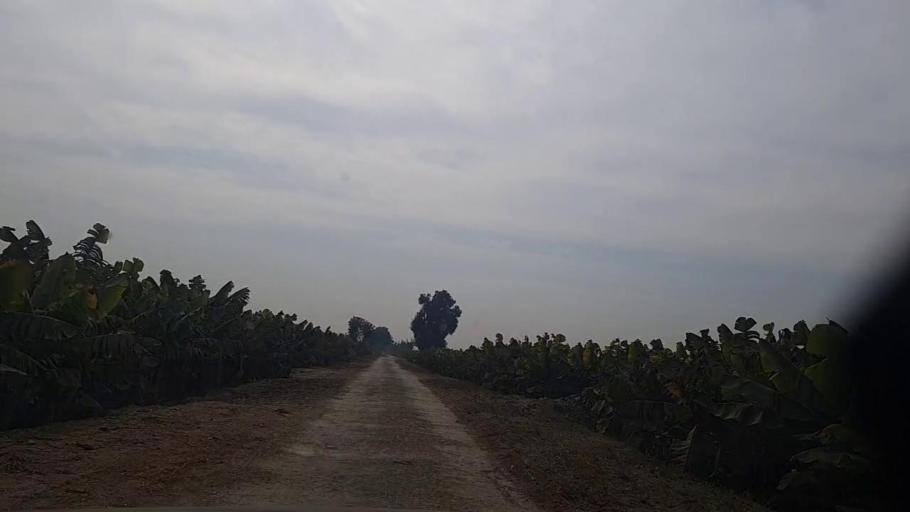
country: PK
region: Sindh
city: Sakrand
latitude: 26.2390
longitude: 68.2972
